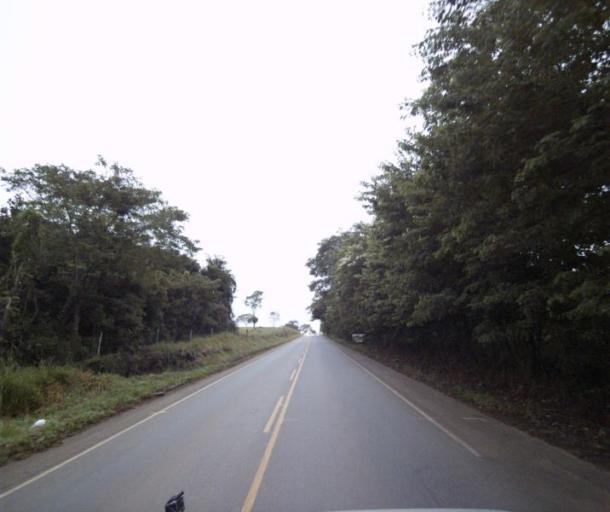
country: BR
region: Goias
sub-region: Pirenopolis
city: Pirenopolis
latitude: -15.9015
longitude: -48.7988
